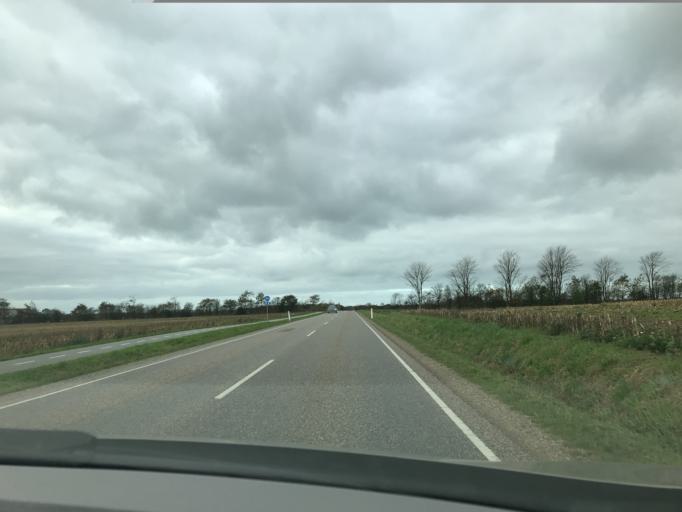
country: DK
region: South Denmark
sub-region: Varde Kommune
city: Olgod
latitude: 55.7948
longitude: 8.6595
